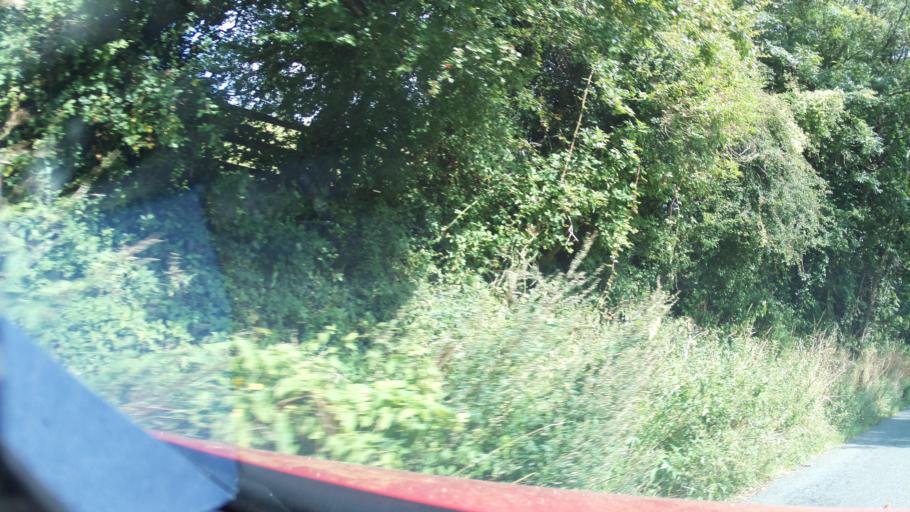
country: GB
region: England
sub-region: Devon
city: Dartmouth
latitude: 50.3574
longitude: -3.5626
